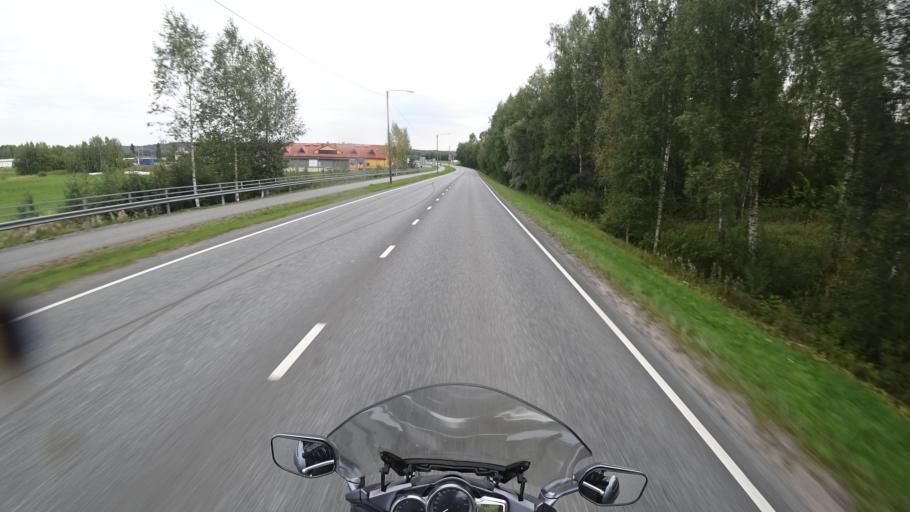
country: FI
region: Uusimaa
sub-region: Raaseporin
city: Karis
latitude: 60.0565
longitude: 23.6447
